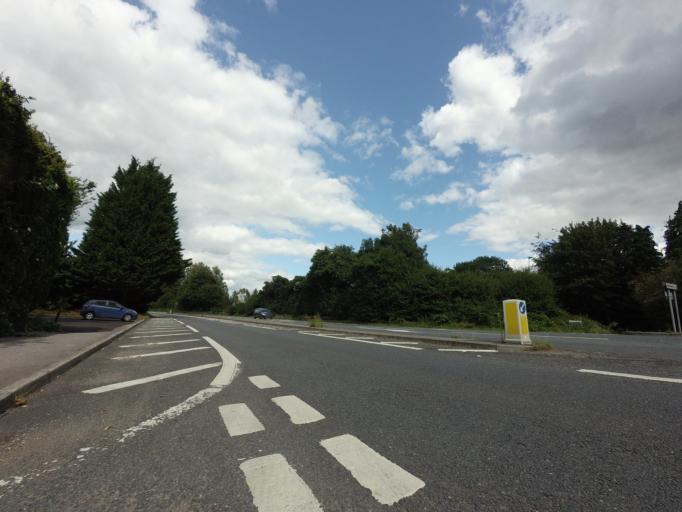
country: GB
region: England
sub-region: Kent
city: Borough Green
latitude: 51.2859
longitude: 0.2816
